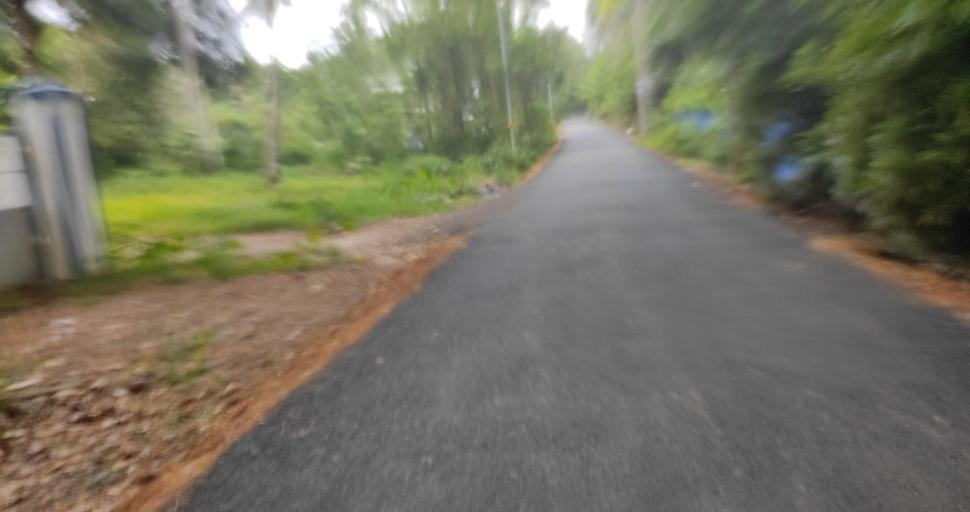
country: IN
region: Kerala
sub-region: Alappuzha
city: Shertallai
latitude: 9.6616
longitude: 76.3318
